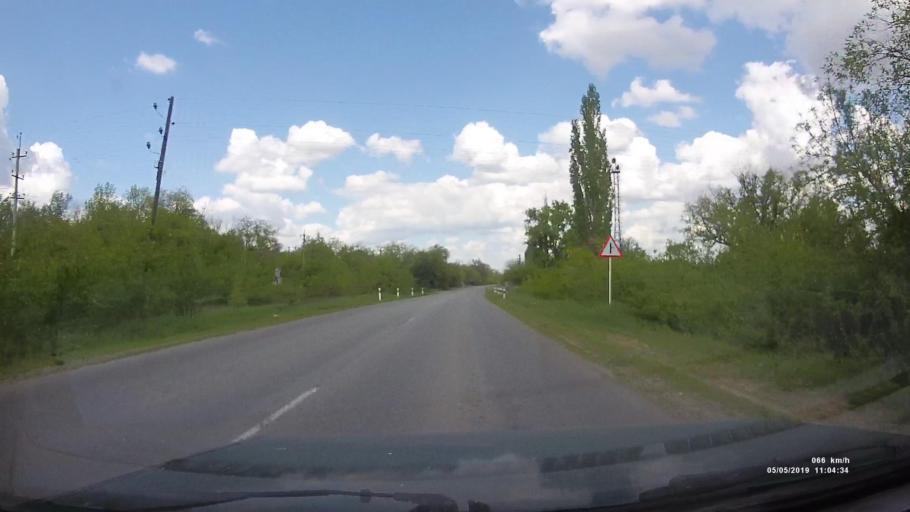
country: RU
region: Rostov
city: Ust'-Donetskiy
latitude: 47.6982
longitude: 40.9170
